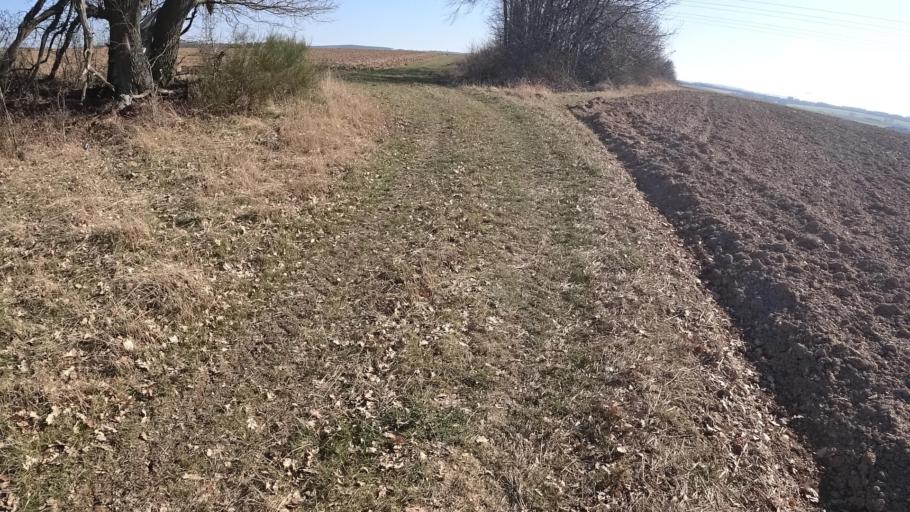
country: DE
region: Rheinland-Pfalz
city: Mutterschied
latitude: 49.9880
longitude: 7.5637
